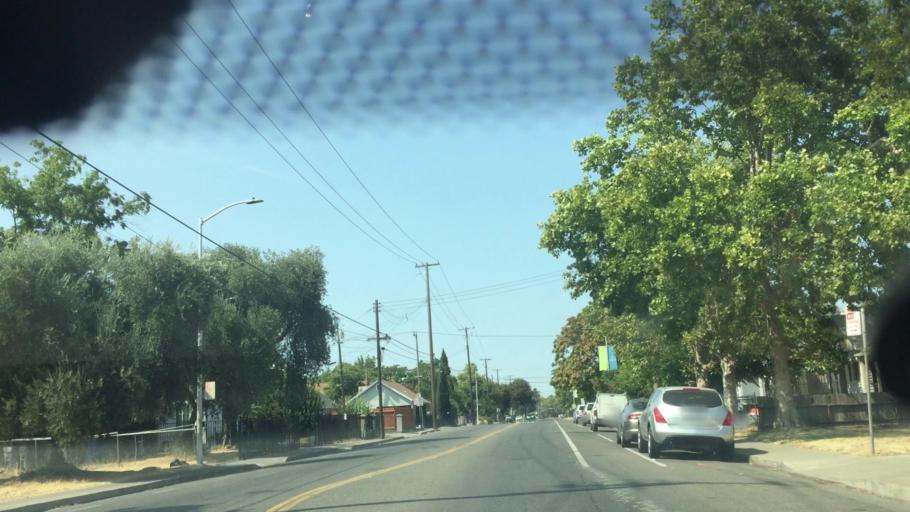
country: US
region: California
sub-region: Sacramento County
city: Parkway
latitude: 38.5398
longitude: -121.4647
